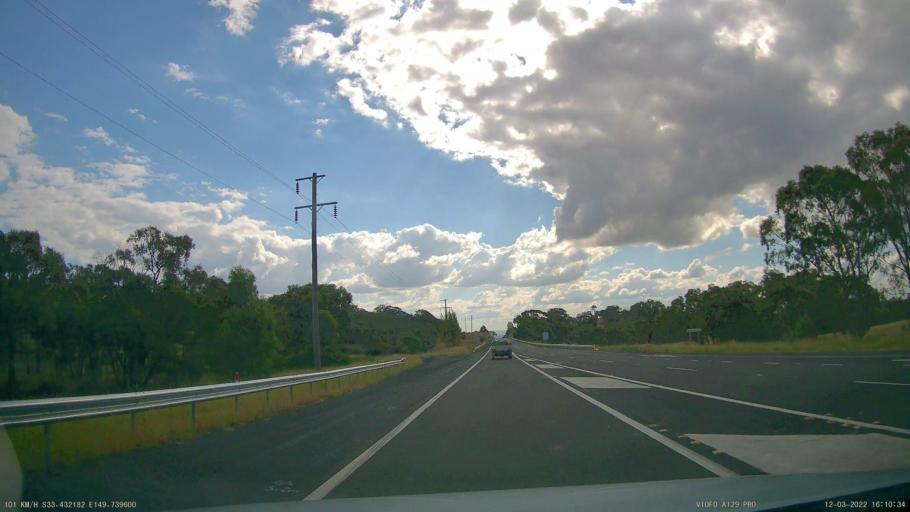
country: AU
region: New South Wales
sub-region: Bathurst Regional
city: Kelso
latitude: -33.4318
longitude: 149.7399
